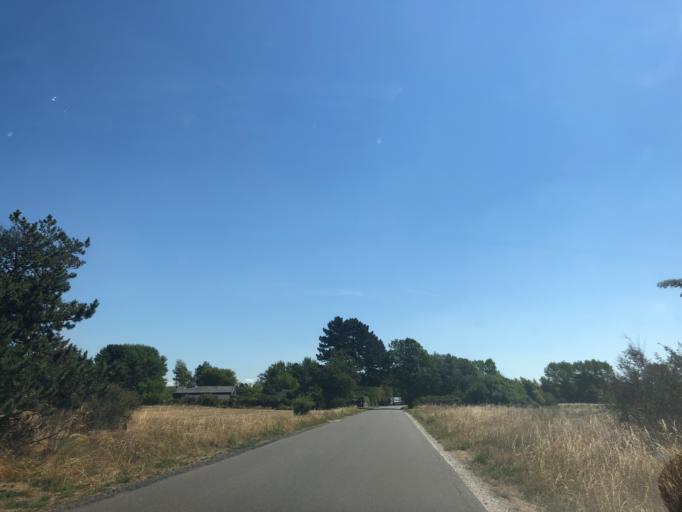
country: DK
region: Zealand
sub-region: Slagelse Kommune
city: Forlev
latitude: 55.3783
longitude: 11.2195
